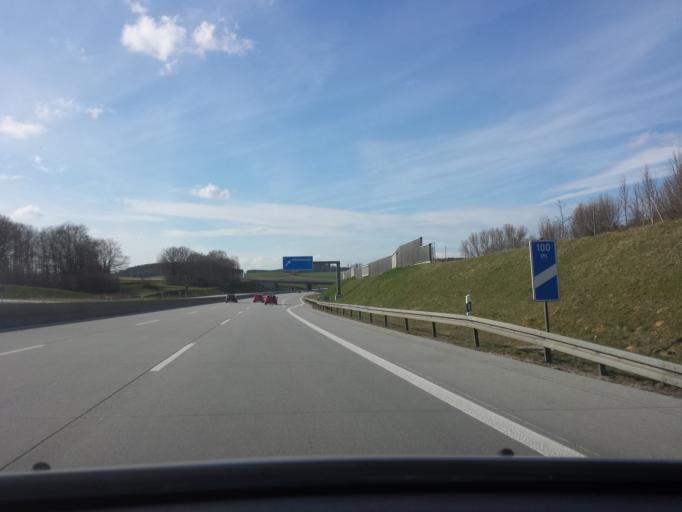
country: DE
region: Bavaria
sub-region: Swabia
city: Adelzhausen
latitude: 48.3488
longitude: 11.1384
